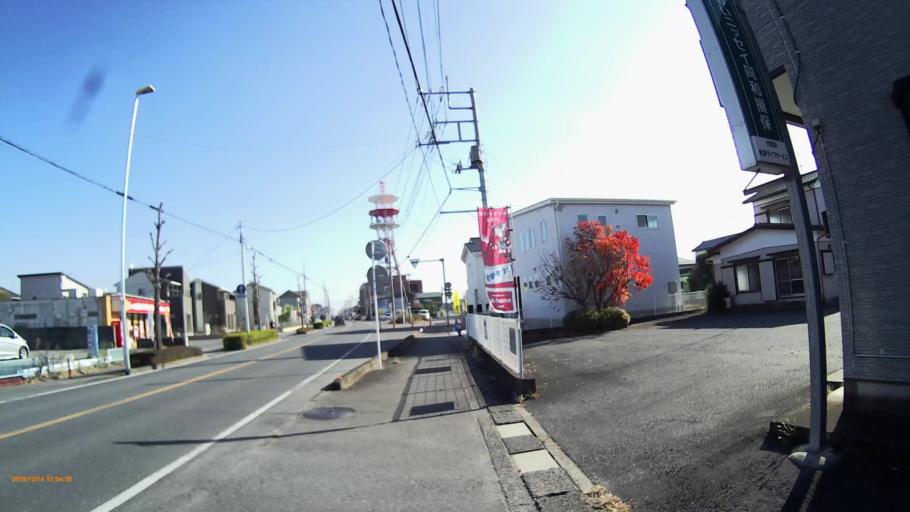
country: JP
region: Saitama
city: Fukiage-fujimi
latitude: 36.1025
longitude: 139.4571
